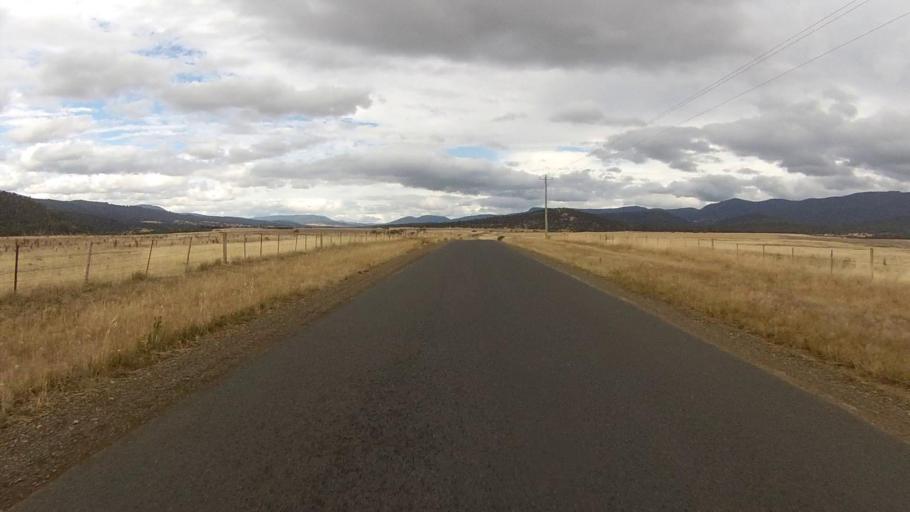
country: AU
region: Tasmania
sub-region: Northern Midlands
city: Evandale
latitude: -41.8247
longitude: 147.7698
